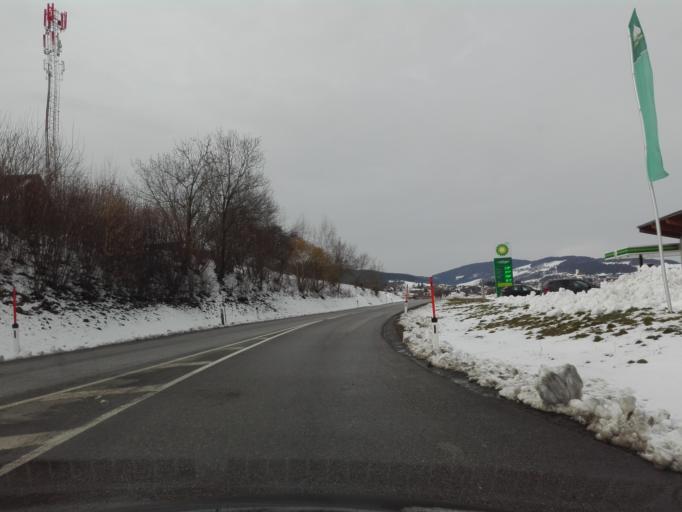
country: AT
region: Upper Austria
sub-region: Politischer Bezirk Rohrbach
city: Atzesberg
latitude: 48.5021
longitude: 13.8834
